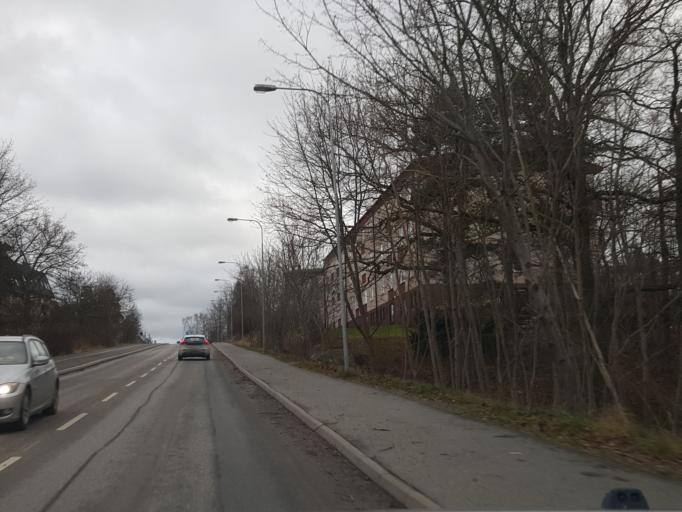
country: SE
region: Stockholm
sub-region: Nacka Kommun
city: Fisksatra
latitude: 59.3093
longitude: 18.2281
